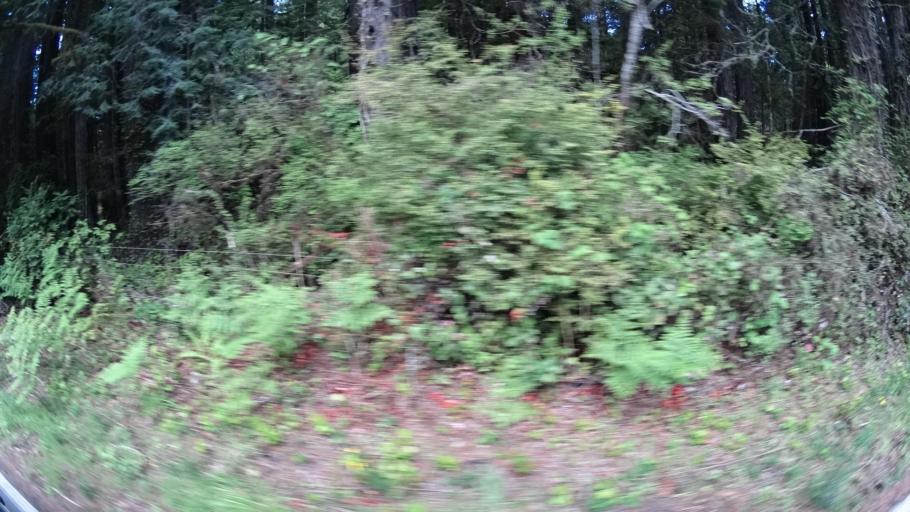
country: US
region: California
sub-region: Humboldt County
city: Blue Lake
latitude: 40.9167
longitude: -124.0229
